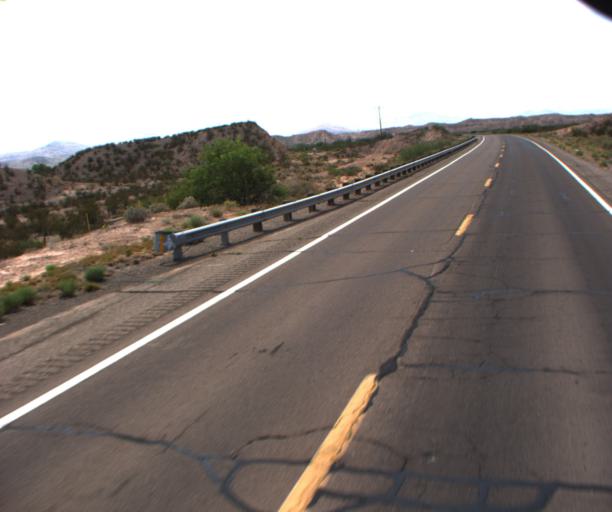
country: US
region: Arizona
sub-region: Greenlee County
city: Clifton
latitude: 32.7473
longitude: -109.1070
